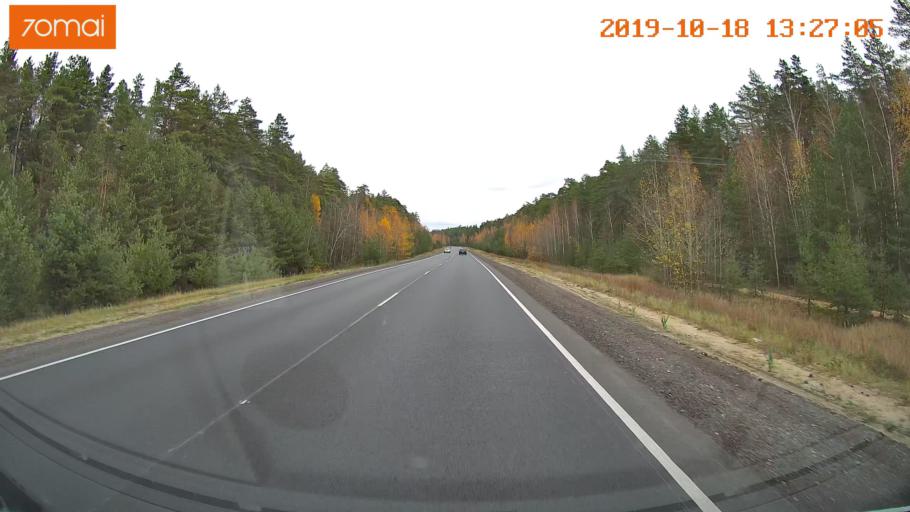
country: RU
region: Rjazan
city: Solotcha
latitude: 54.7600
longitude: 39.8478
